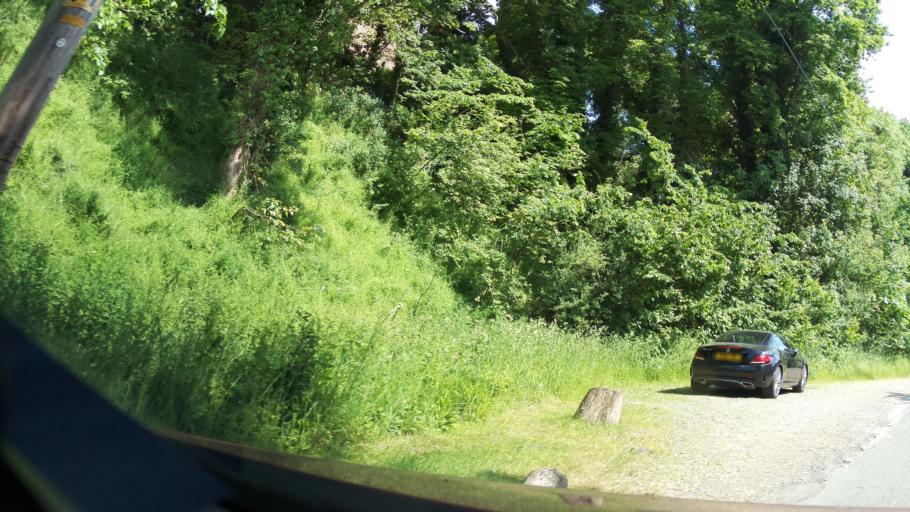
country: GB
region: England
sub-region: Wiltshire
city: Rushall
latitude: 51.2650
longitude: -1.7967
